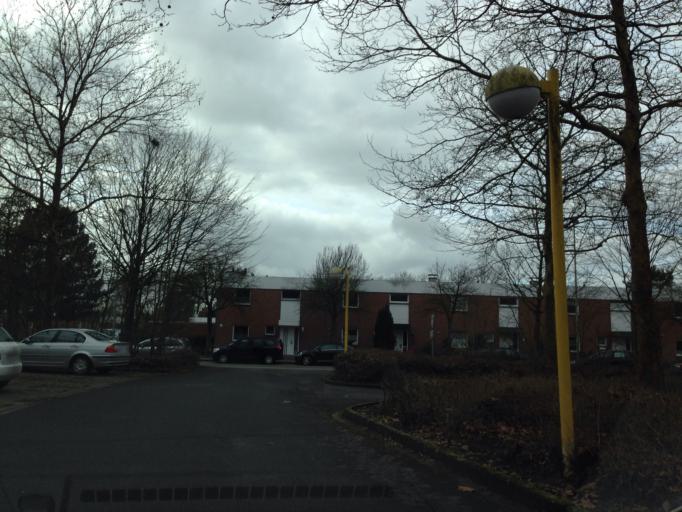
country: DE
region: North Rhine-Westphalia
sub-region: Regierungsbezirk Munster
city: Muenster
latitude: 51.9996
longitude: 7.6039
